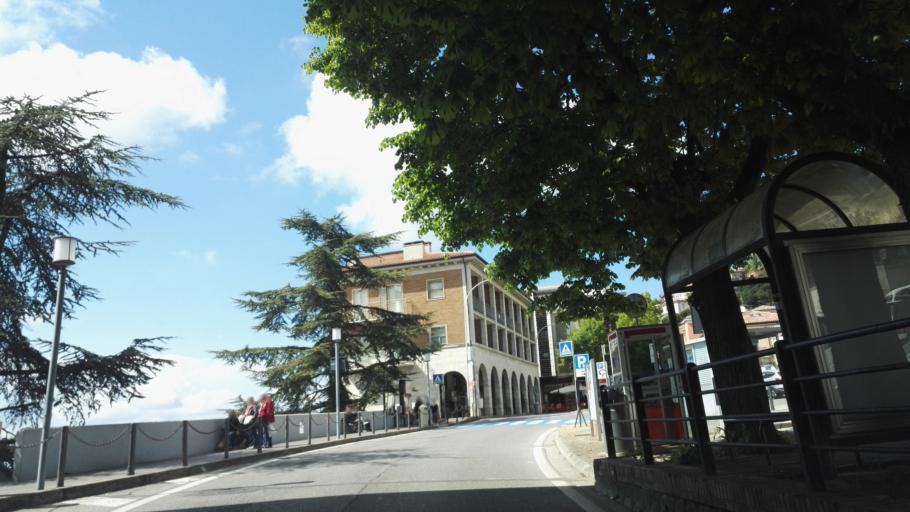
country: SM
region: San Marino
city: San Marino
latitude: 43.9313
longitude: 12.4488
